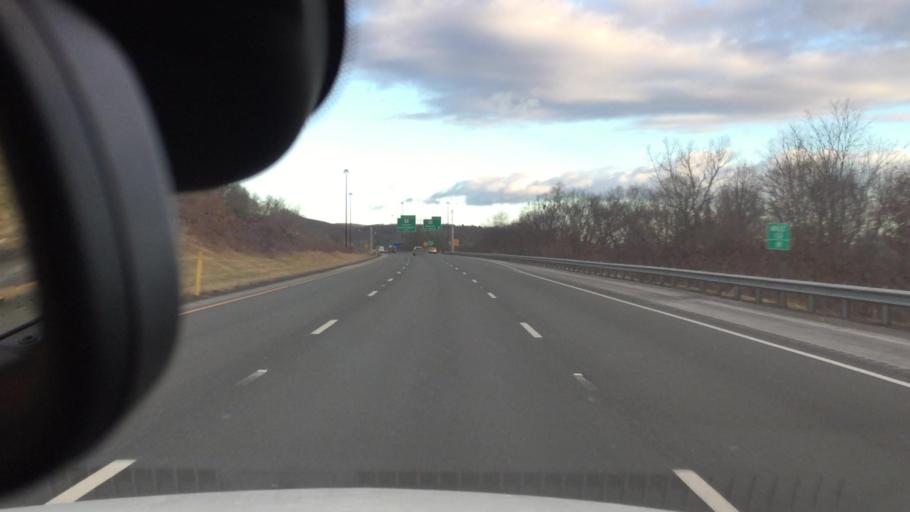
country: US
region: Massachusetts
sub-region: Hampden County
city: Holyoke
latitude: 42.1939
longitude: -72.6377
